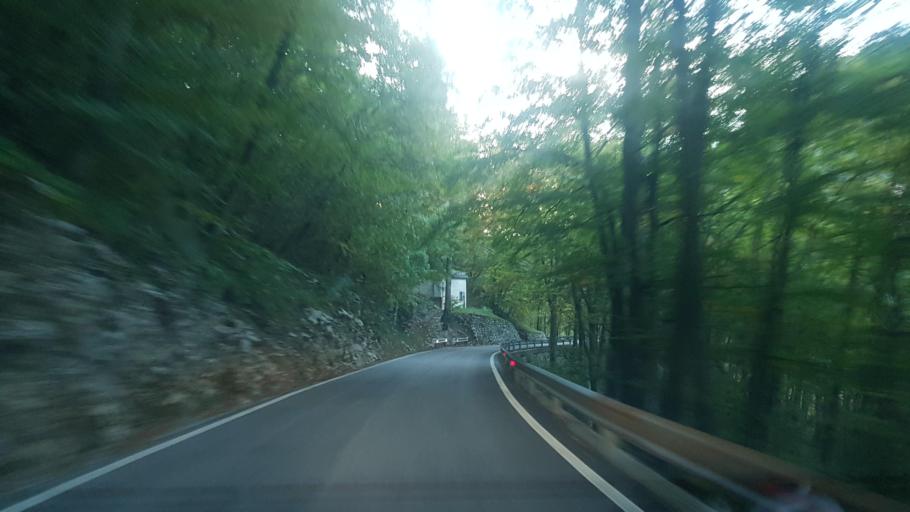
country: IT
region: Friuli Venezia Giulia
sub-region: Provincia di Udine
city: Villa Santina
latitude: 46.3503
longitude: 12.9151
